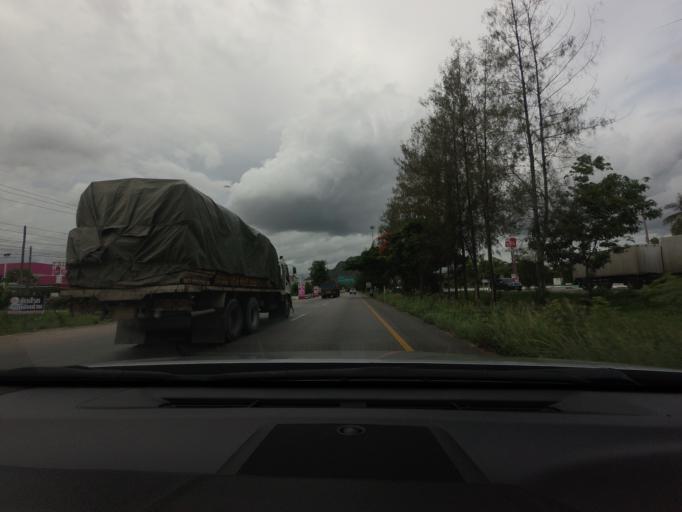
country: TH
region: Phetchaburi
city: Cha-am
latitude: 12.7987
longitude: 99.9414
